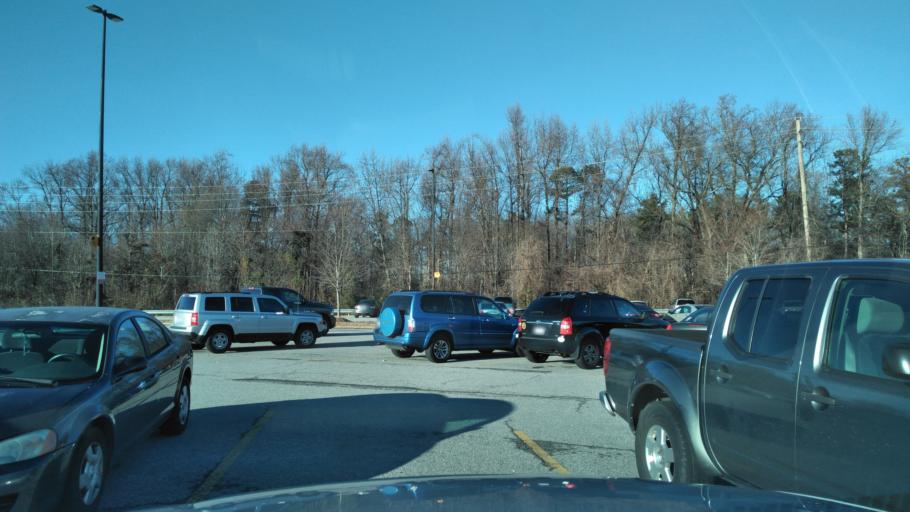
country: US
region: South Carolina
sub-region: Greenville County
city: Mauldin
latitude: 34.8233
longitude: -82.2829
